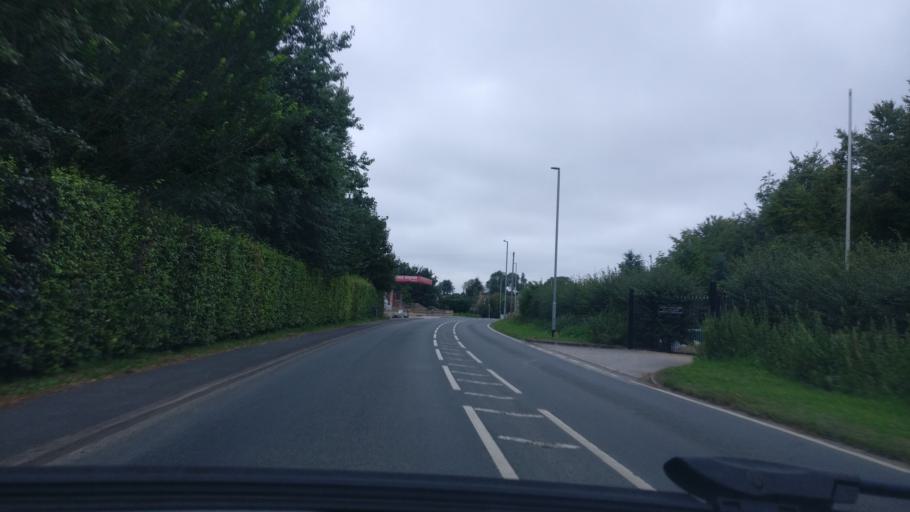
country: GB
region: England
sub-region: East Riding of Yorkshire
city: Leven
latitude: 53.8854
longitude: -0.3150
